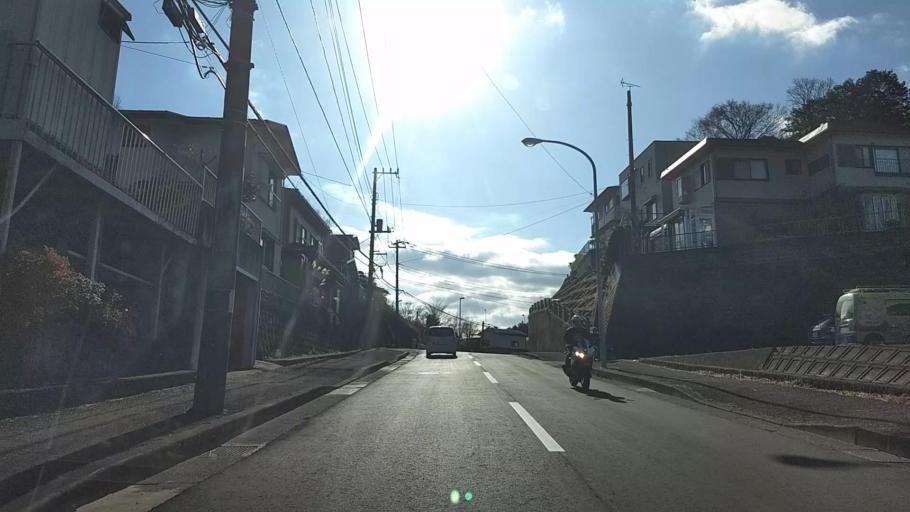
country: JP
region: Kanagawa
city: Atsugi
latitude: 35.4713
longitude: 139.2873
